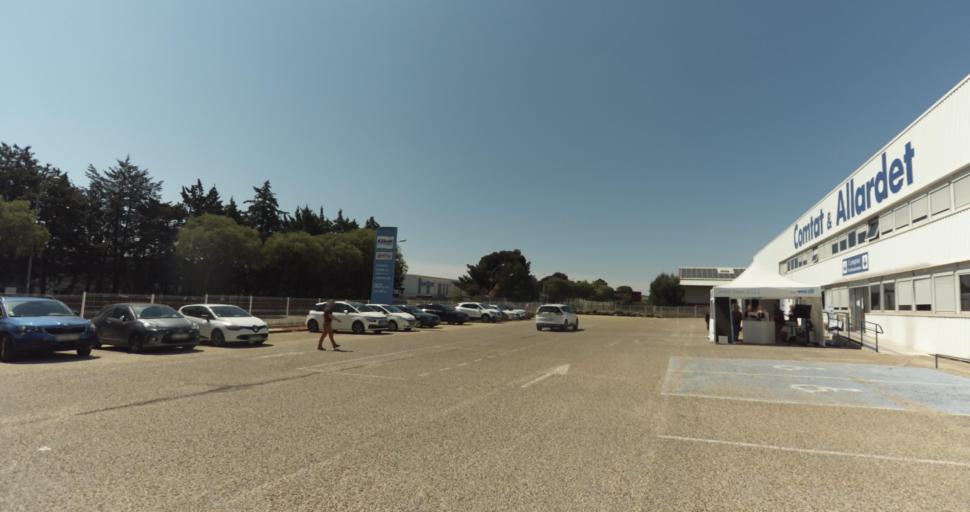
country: FR
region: Languedoc-Roussillon
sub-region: Departement du Gard
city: Milhaud
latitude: 43.8093
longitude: 4.3178
